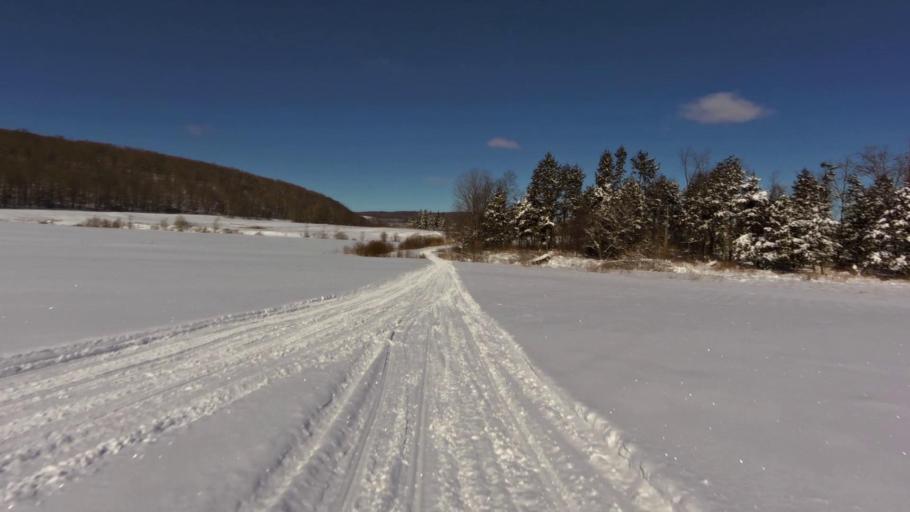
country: US
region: New York
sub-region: Chautauqua County
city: Fredonia
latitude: 42.3493
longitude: -79.1737
